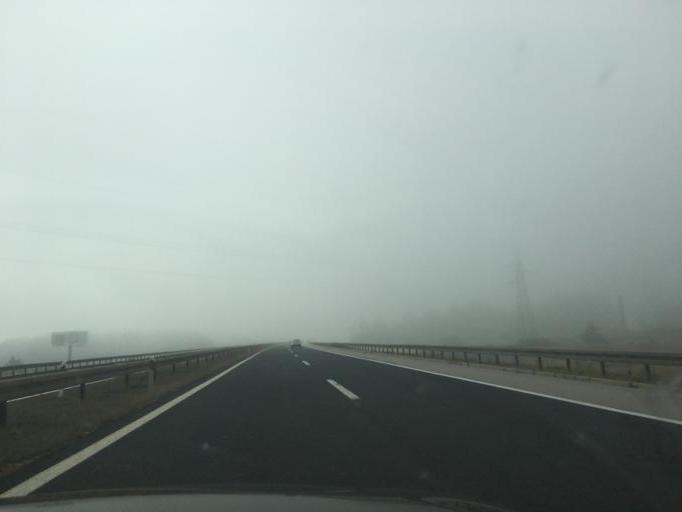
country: HR
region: Licko-Senjska
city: Gospic
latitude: 44.6023
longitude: 15.4394
